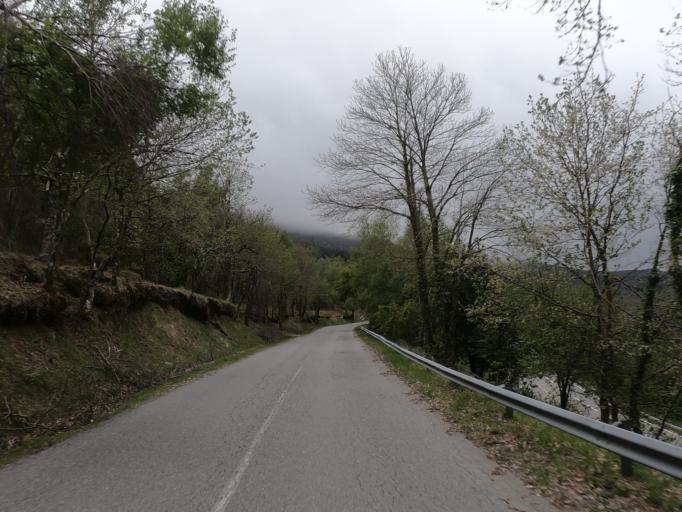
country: PT
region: Vila Real
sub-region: Santa Marta de Penaguiao
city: Santa Marta de Penaguiao
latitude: 41.2785
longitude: -7.8864
